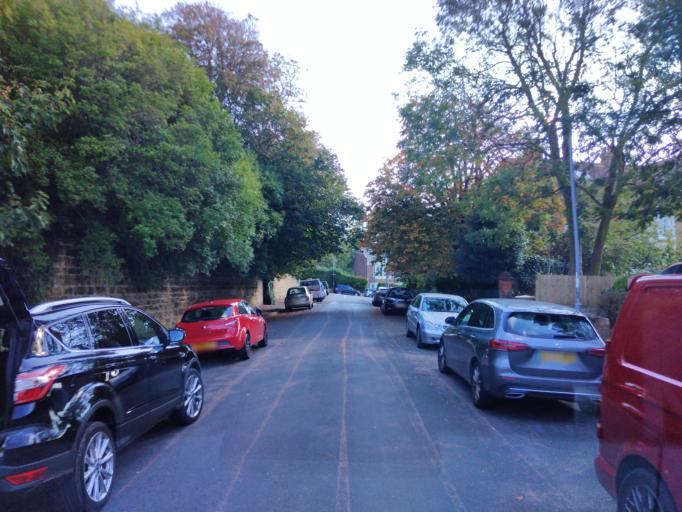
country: GB
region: England
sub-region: East Sussex
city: Hastings
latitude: 50.8608
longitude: 0.5604
